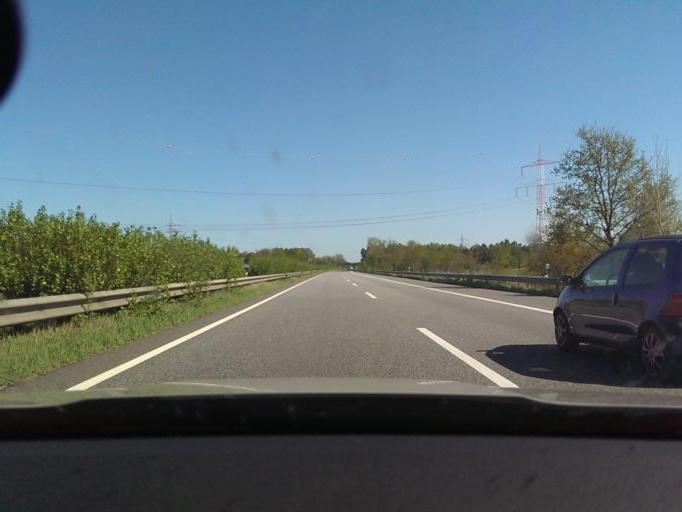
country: DE
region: Lower Saxony
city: Langwedel
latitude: 52.9895
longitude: 9.2019
